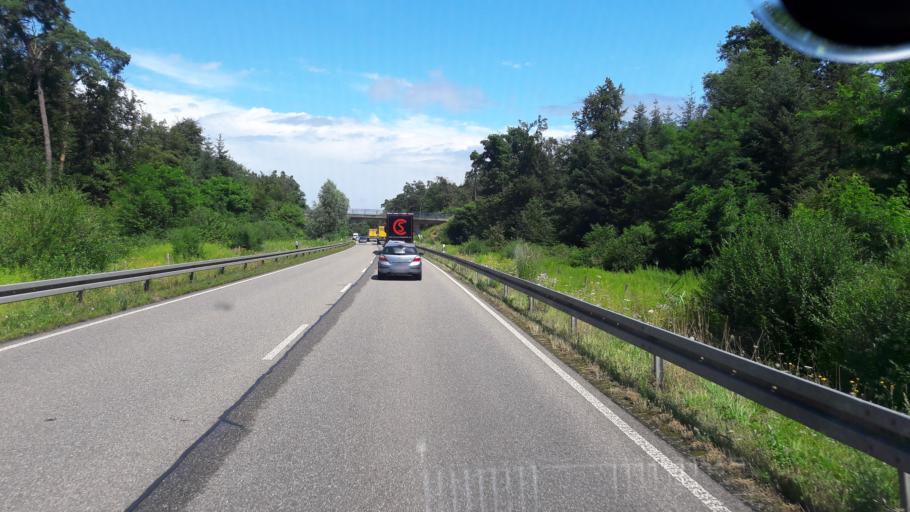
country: DE
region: Baden-Wuerttemberg
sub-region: Karlsruhe Region
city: Graben-Neudorf
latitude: 49.1426
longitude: 8.4921
